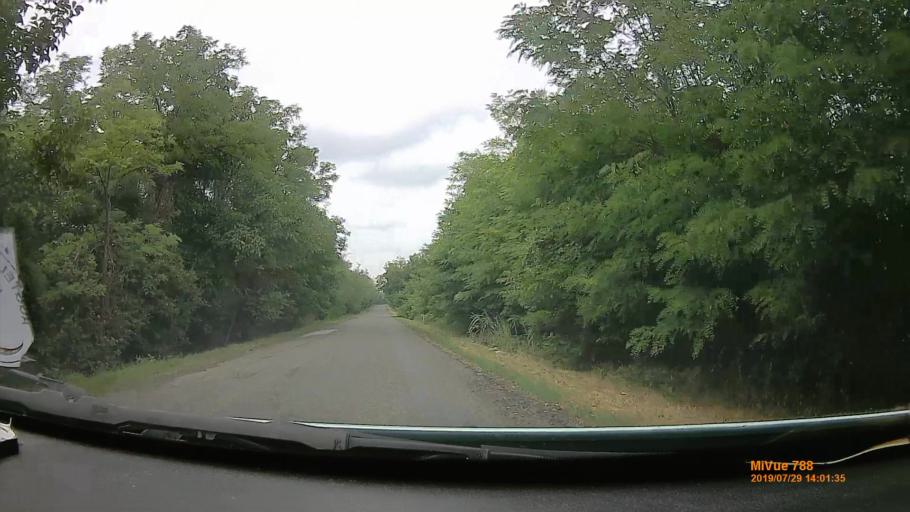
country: HU
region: Somogy
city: Balatonfoldvar
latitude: 46.7973
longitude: 17.9363
